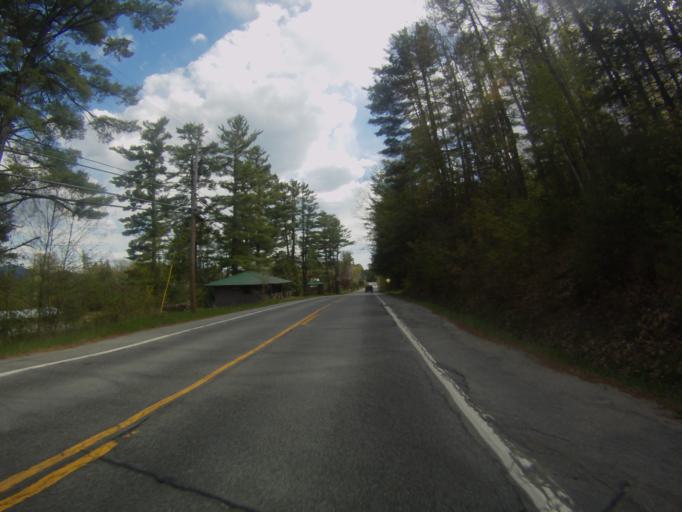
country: US
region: New York
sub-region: Essex County
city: Mineville
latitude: 43.8788
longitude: -73.7502
